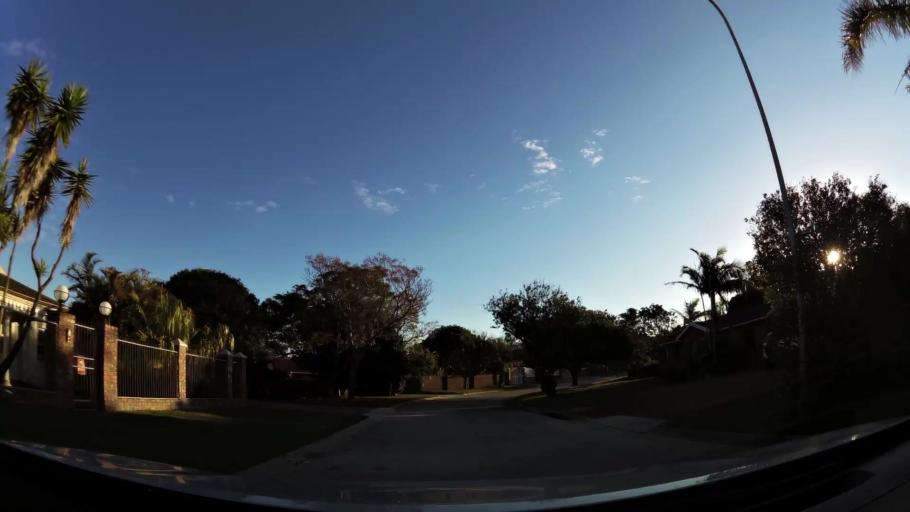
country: ZA
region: Eastern Cape
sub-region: Nelson Mandela Bay Metropolitan Municipality
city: Port Elizabeth
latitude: -33.9777
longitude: 25.4923
